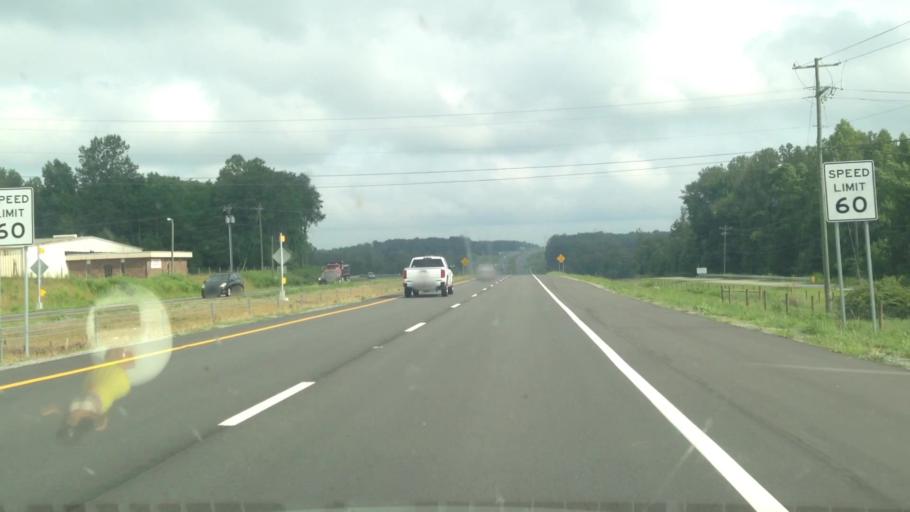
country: US
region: North Carolina
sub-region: Guilford County
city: Summerfield
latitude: 36.2217
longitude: -79.9107
